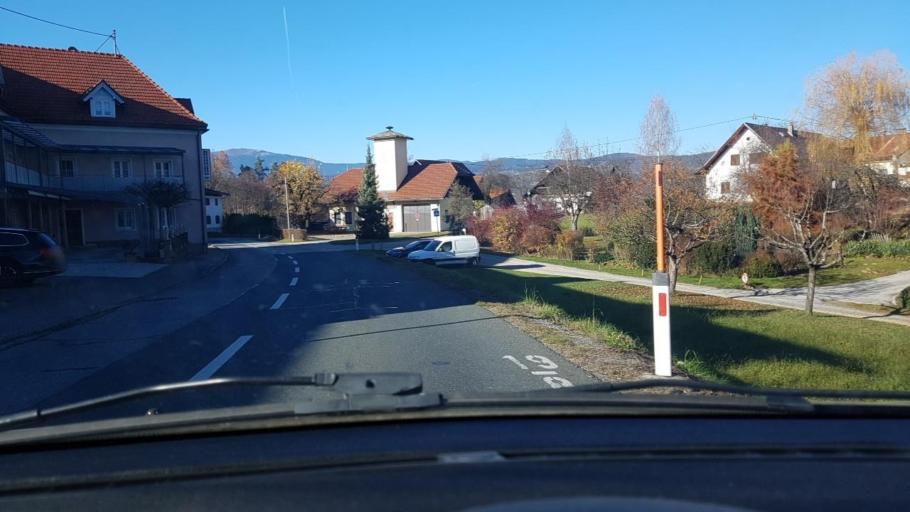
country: AT
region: Carinthia
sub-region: Politischer Bezirk Villach Land
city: Velden am Woerthersee
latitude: 46.6005
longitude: 14.0629
